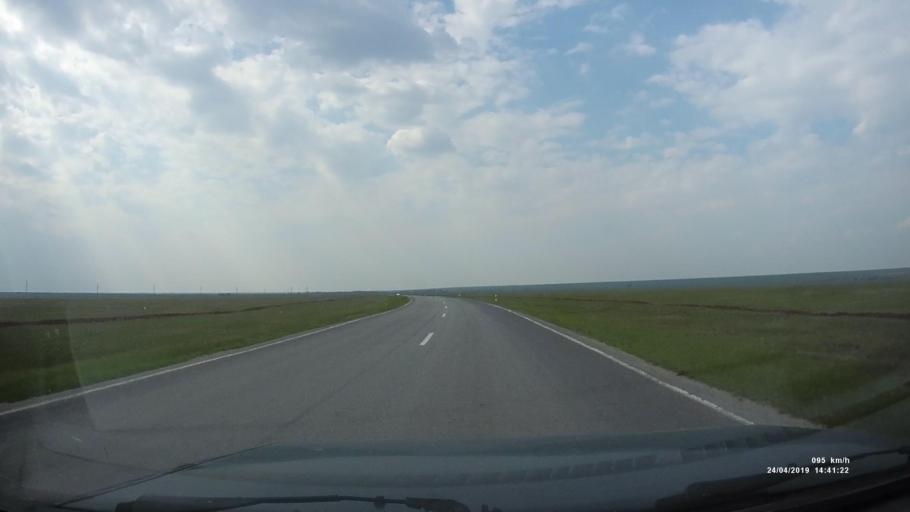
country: RU
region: Rostov
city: Remontnoye
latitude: 46.4445
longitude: 43.8806
